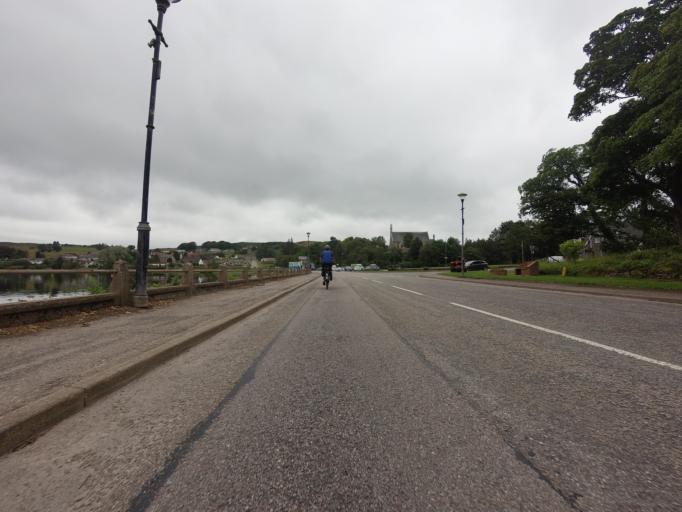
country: GB
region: Scotland
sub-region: Highland
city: Alness
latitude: 58.0239
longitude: -4.4023
